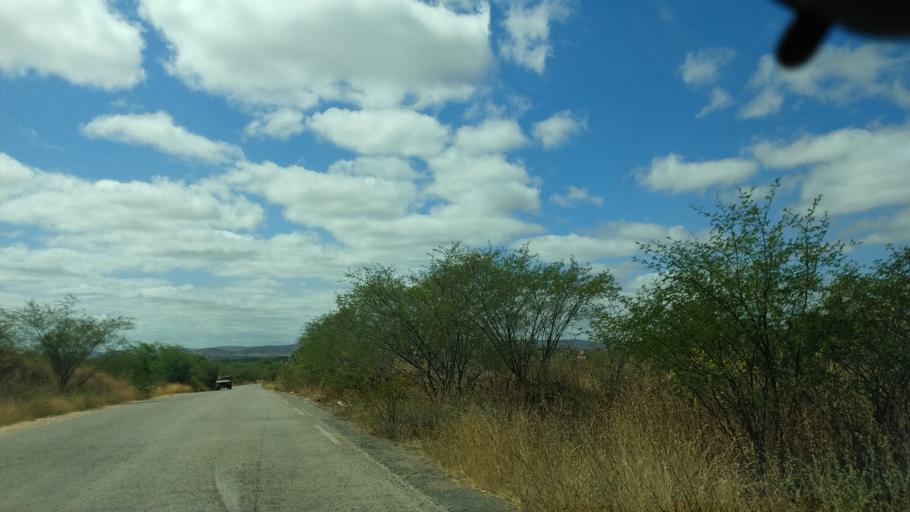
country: BR
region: Rio Grande do Norte
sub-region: Currais Novos
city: Currais Novos
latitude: -6.2611
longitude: -36.5710
